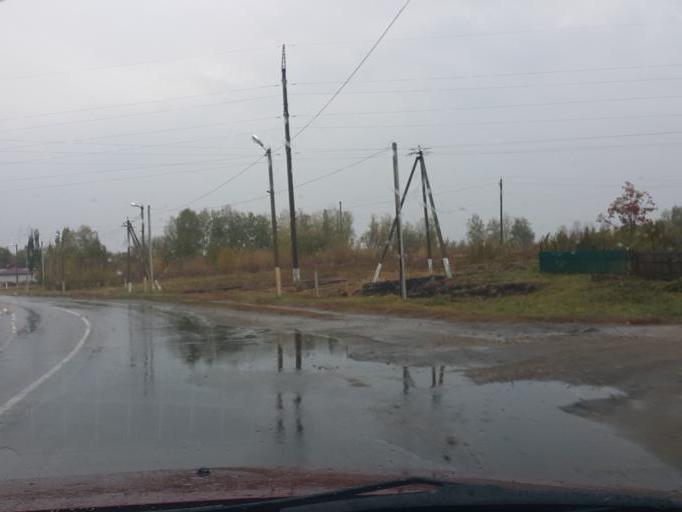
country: RU
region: Tambov
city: Znamenka
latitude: 52.4061
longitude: 41.4605
